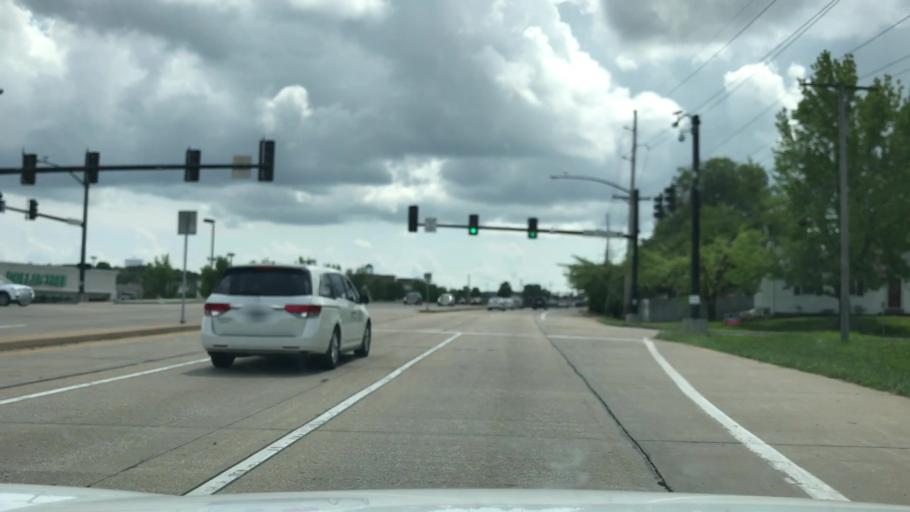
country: US
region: Missouri
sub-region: Saint Charles County
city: O'Fallon
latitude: 38.7875
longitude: -90.7000
